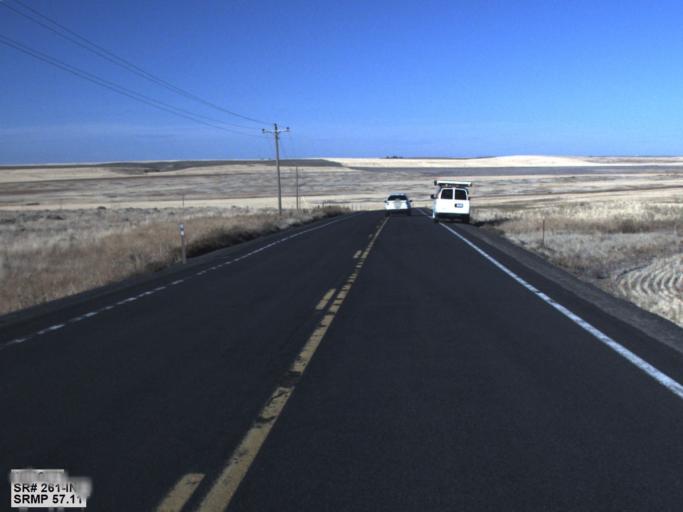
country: US
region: Washington
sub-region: Adams County
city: Ritzville
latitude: 47.0378
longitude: -118.3482
